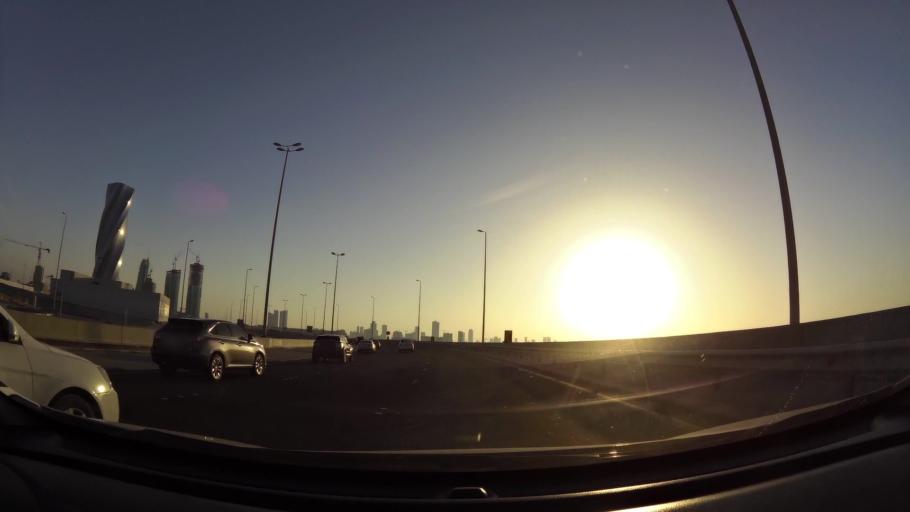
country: BH
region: Muharraq
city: Al Muharraq
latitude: 26.2528
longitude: 50.5789
